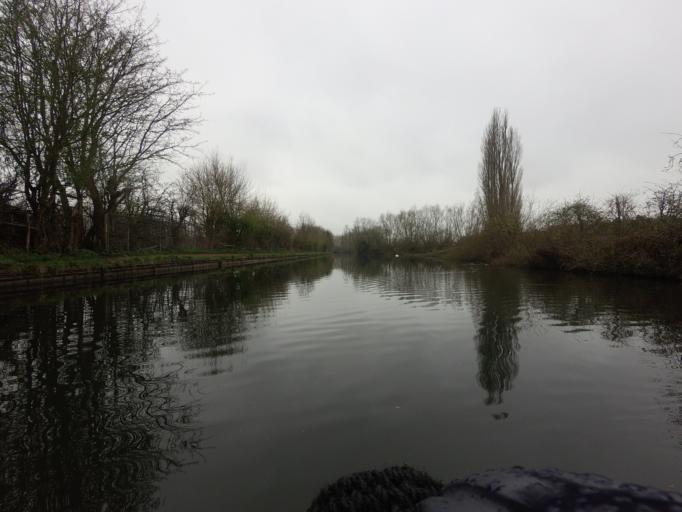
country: GB
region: England
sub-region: Hertfordshire
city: Kings Langley
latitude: 51.7212
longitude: -0.4493
